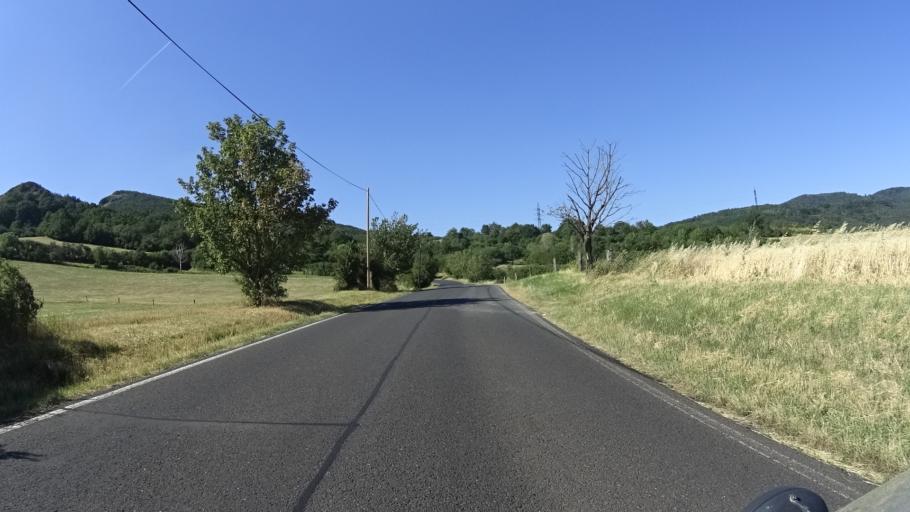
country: CZ
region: Ustecky
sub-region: Okres Litomerice
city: Litomerice
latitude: 50.5608
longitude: 14.1216
